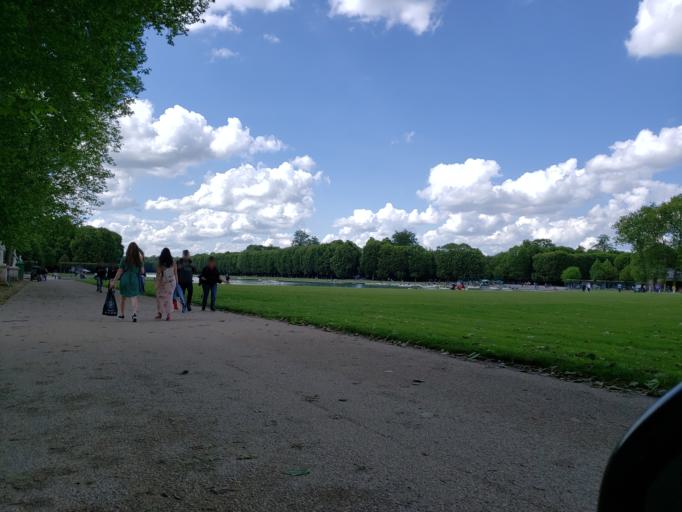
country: FR
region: Ile-de-France
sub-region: Departement des Yvelines
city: Le Chesnay
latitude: 48.8068
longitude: 2.1095
